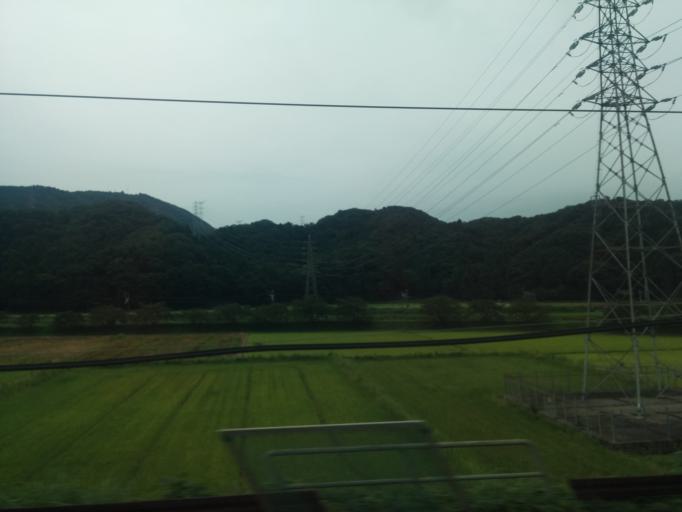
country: JP
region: Shiga Prefecture
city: Nagahama
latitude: 35.3654
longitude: 136.3844
